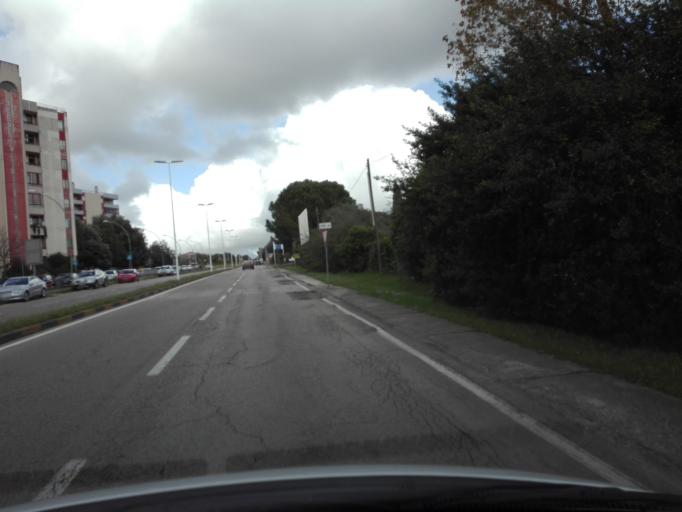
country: IT
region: Sardinia
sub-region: Provincia di Sassari
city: Sassari
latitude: 40.7111
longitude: 8.5801
